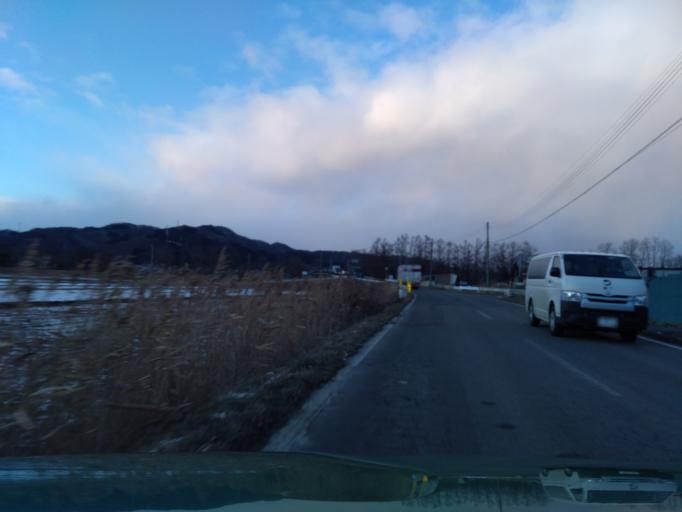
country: JP
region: Iwate
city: Shizukuishi
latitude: 39.6941
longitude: 141.0650
